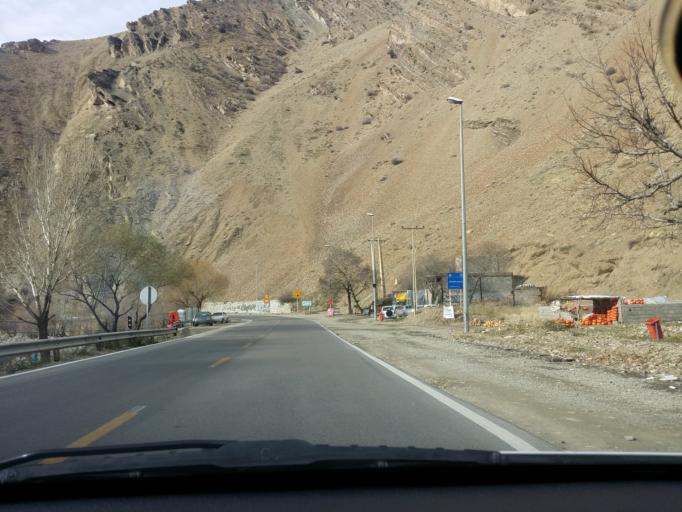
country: IR
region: Alborz
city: Karaj
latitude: 36.0377
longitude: 51.1807
